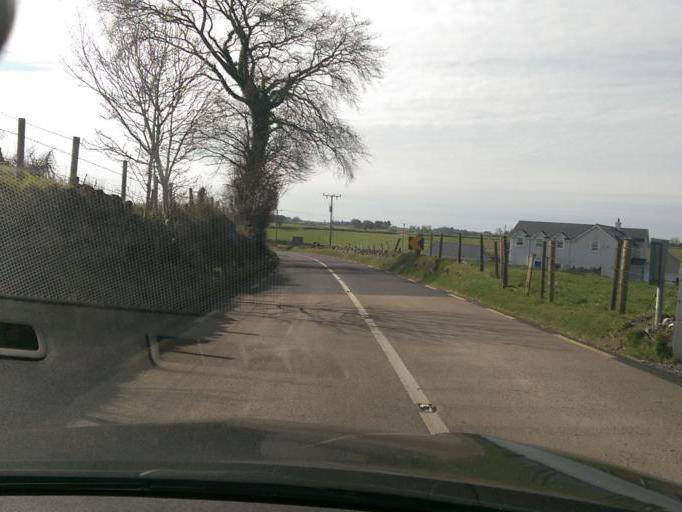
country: IE
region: Connaught
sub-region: County Galway
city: Athenry
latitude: 53.4881
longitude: -8.5816
